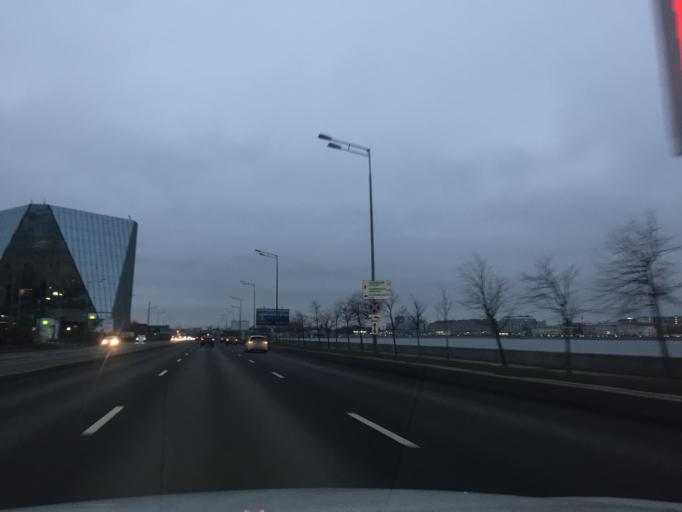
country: RU
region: St.-Petersburg
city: Centralniy
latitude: 59.9360
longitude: 30.4022
